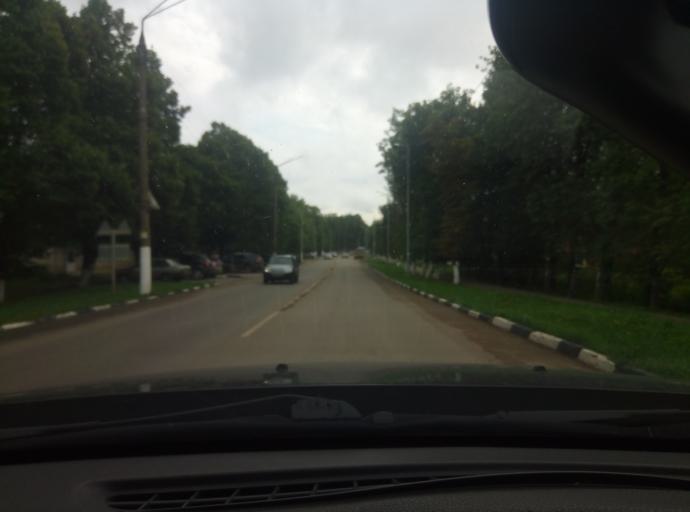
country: RU
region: Tula
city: Donskoy
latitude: 53.9684
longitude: 38.3253
